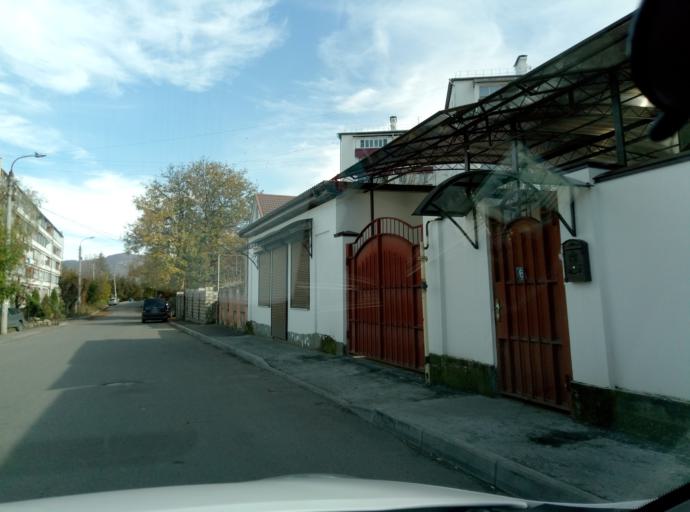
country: RU
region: Stavropol'skiy
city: Kislovodsk
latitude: 43.9053
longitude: 42.7109
